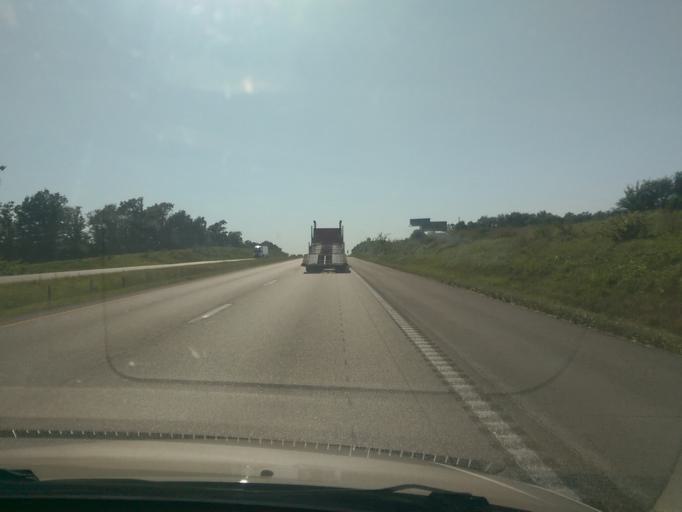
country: US
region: Missouri
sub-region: Saline County
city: Sweet Springs
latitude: 38.9749
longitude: -93.3694
